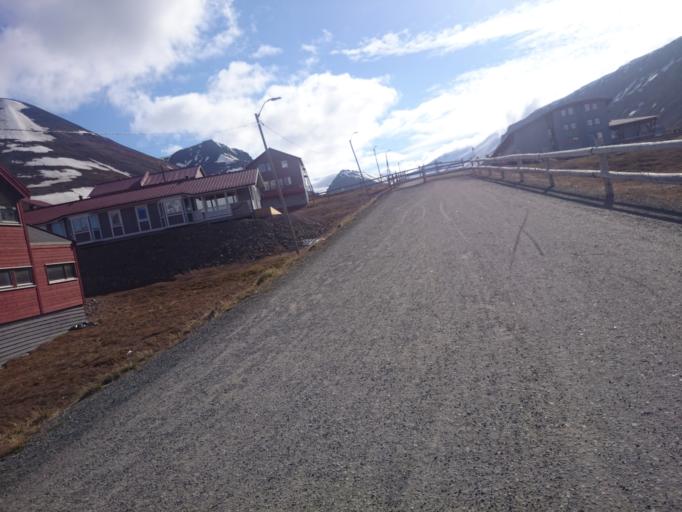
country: SJ
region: Svalbard
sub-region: Spitsbergen
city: Longyearbyen
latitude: 78.2212
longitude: 15.6539
